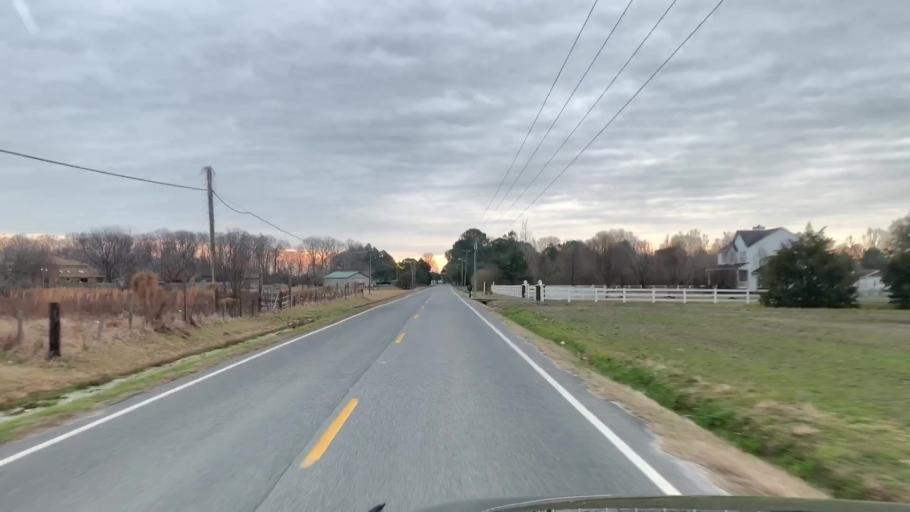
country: US
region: North Carolina
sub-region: Currituck County
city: Moyock
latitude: 36.6258
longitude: -76.1634
